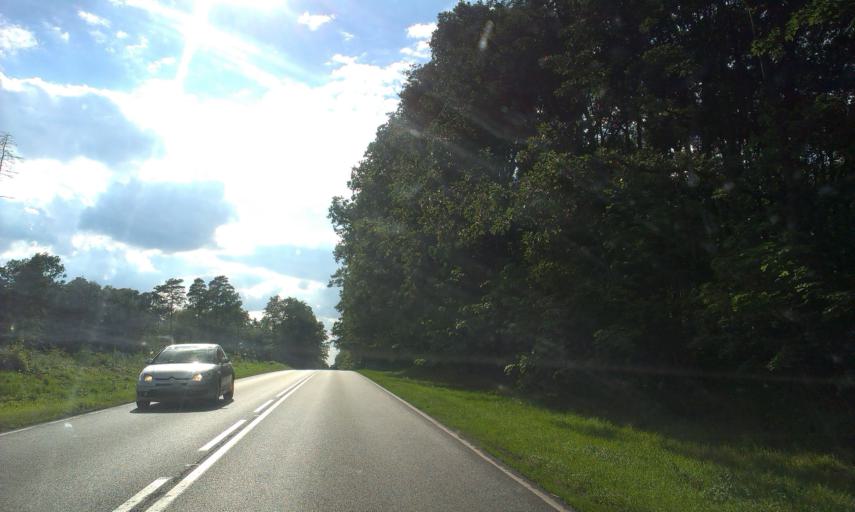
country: PL
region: Greater Poland Voivodeship
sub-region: Powiat pilski
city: Miasteczko Krajenskie
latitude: 53.1332
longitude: 16.9865
